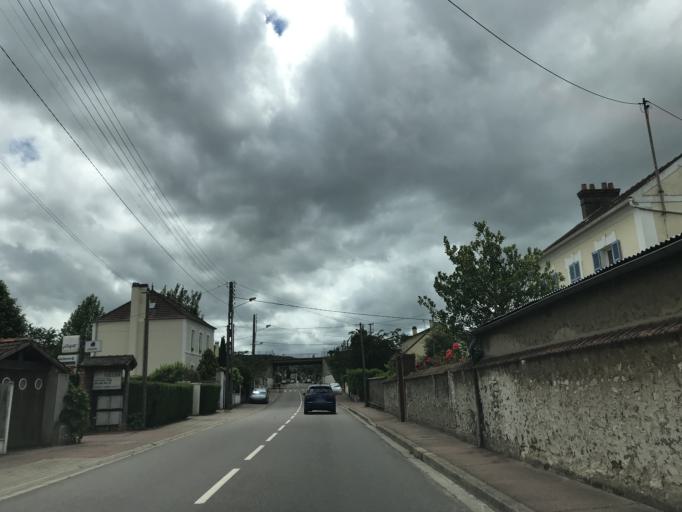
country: FR
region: Ile-de-France
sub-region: Departement des Yvelines
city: Rosny-sur-Seine
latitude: 48.9998
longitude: 1.6275
